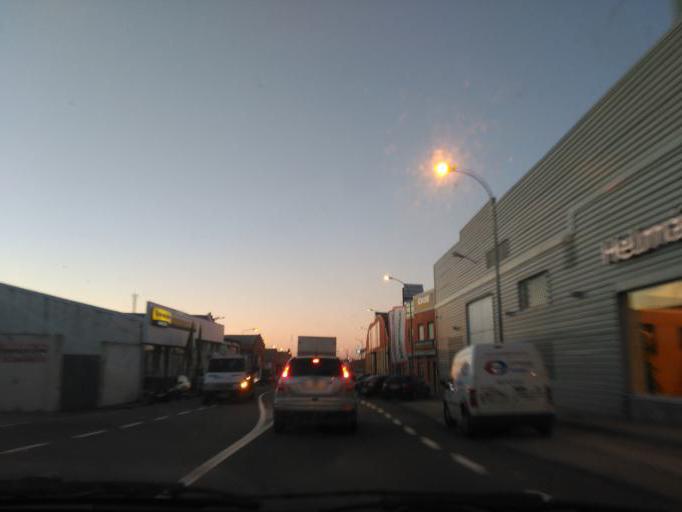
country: ES
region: Castille and Leon
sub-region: Provincia de Salamanca
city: Villares de la Reina
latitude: 40.9910
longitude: -5.6442
